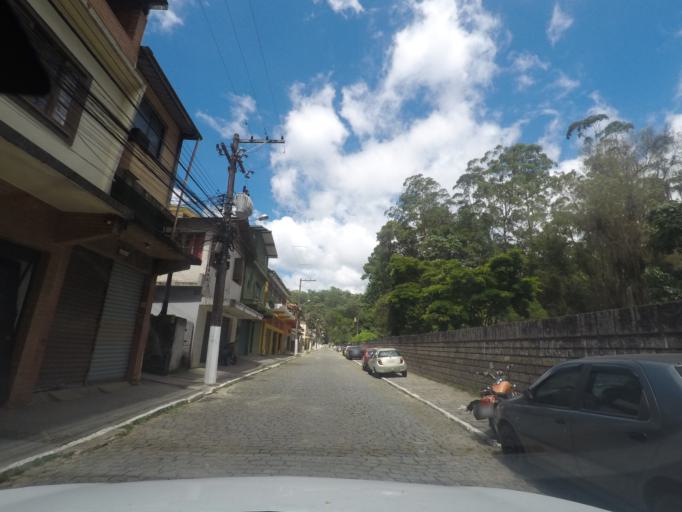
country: BR
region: Rio de Janeiro
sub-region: Teresopolis
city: Teresopolis
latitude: -22.4109
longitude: -42.9828
